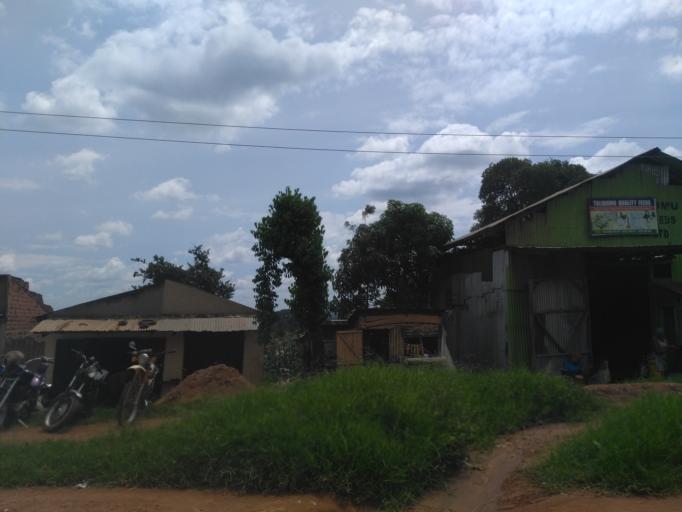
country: UG
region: Central Region
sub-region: Wakiso District
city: Bweyogerere
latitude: 0.4608
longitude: 32.6193
